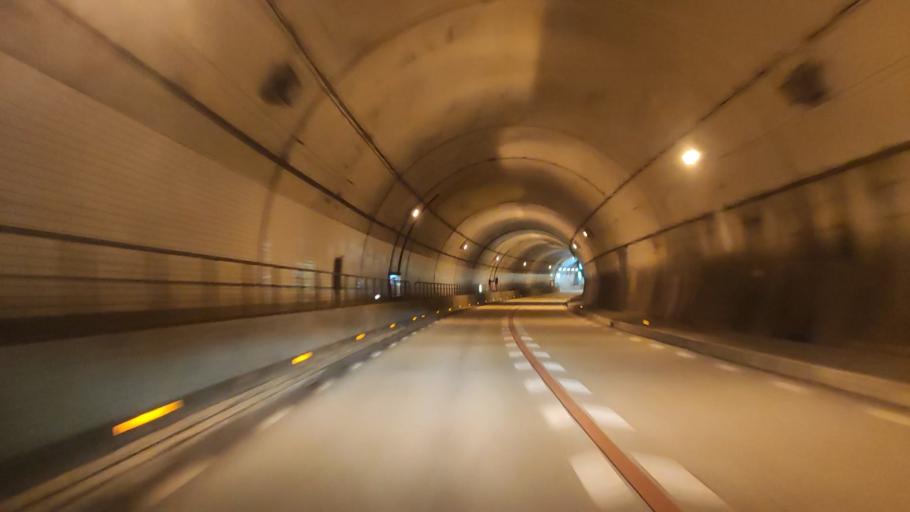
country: JP
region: Hyogo
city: Akashi
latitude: 34.6691
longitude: 135.0618
